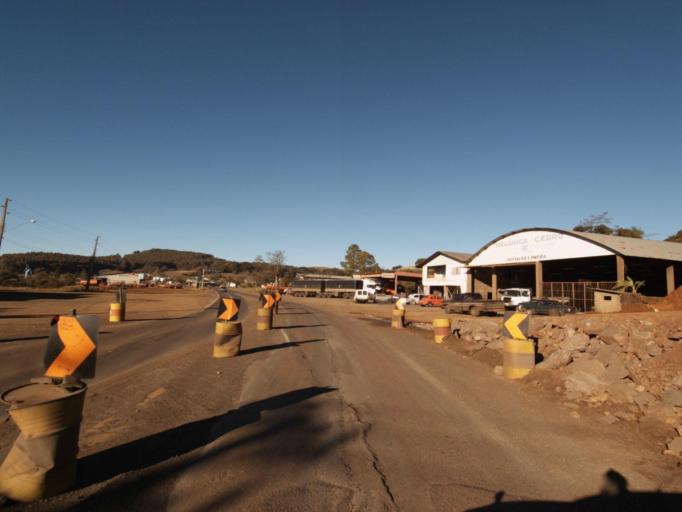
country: AR
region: Misiones
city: Bernardo de Irigoyen
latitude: -26.4551
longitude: -53.5104
